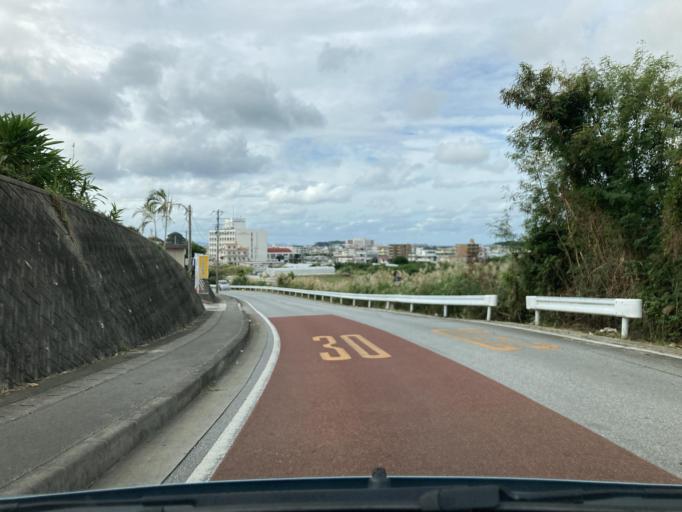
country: JP
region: Okinawa
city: Tomigusuku
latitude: 26.1618
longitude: 127.6725
